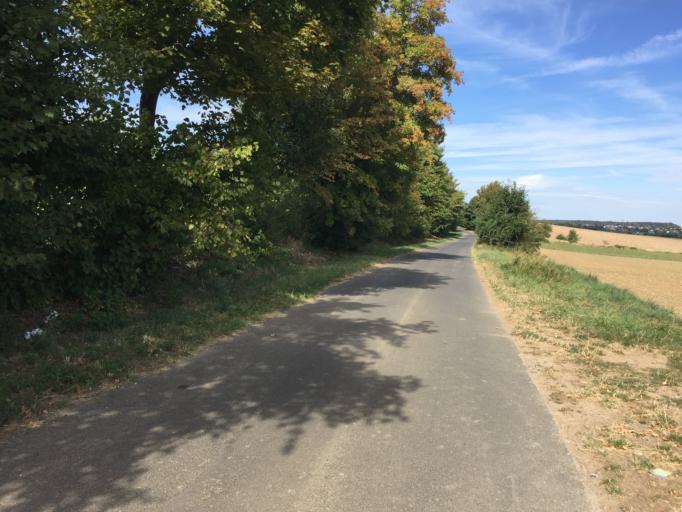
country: DE
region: Hesse
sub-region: Regierungsbezirk Giessen
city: Langgons
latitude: 50.4757
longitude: 8.6558
